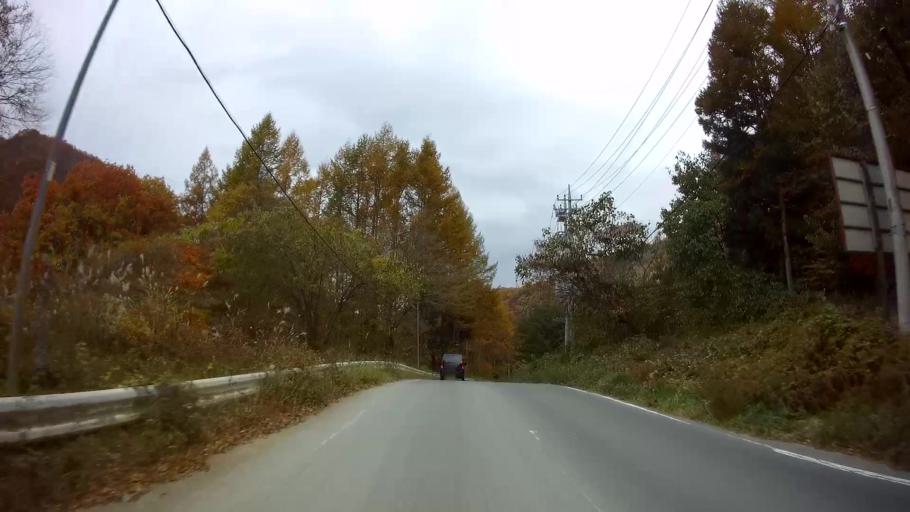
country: JP
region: Gunma
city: Nakanojomachi
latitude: 36.6277
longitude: 138.6499
